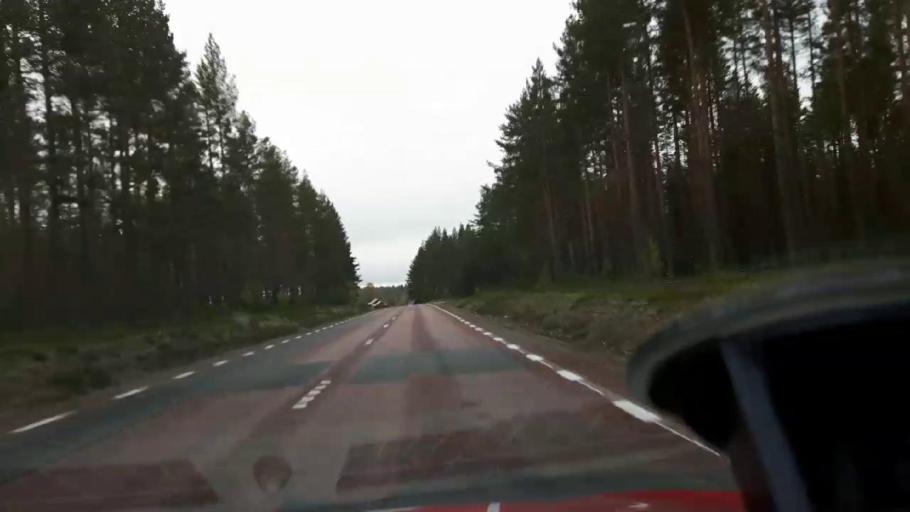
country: SE
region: Gaevleborg
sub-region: Ljusdals Kommun
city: Farila
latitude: 61.8446
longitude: 15.7509
